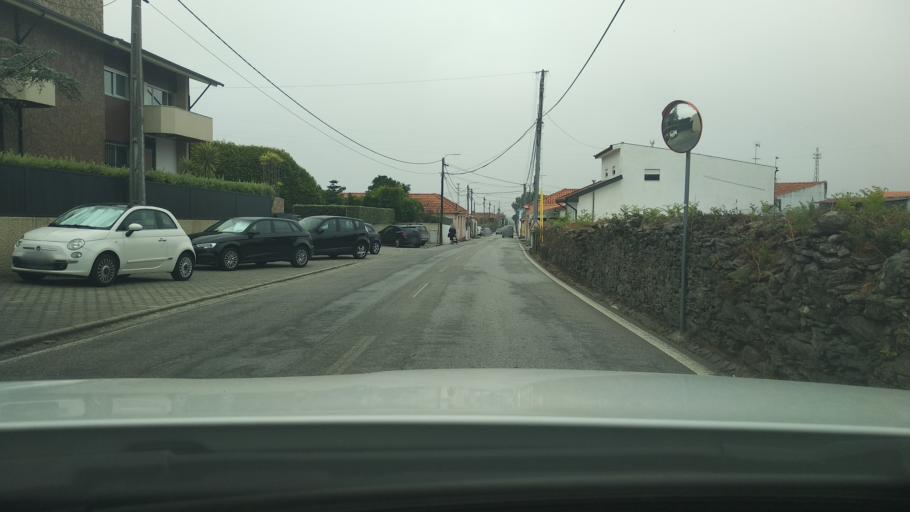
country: PT
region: Aveiro
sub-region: Espinho
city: Souto
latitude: 40.9852
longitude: -8.6233
